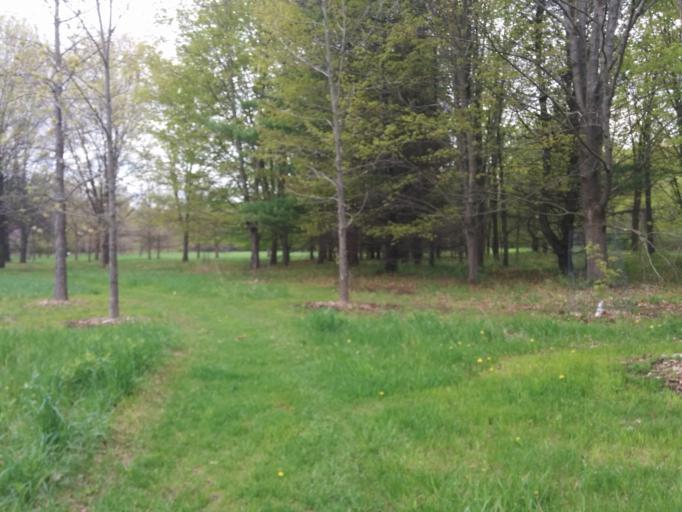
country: US
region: Michigan
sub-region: Midland County
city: Midland
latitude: 43.6033
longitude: -84.2903
